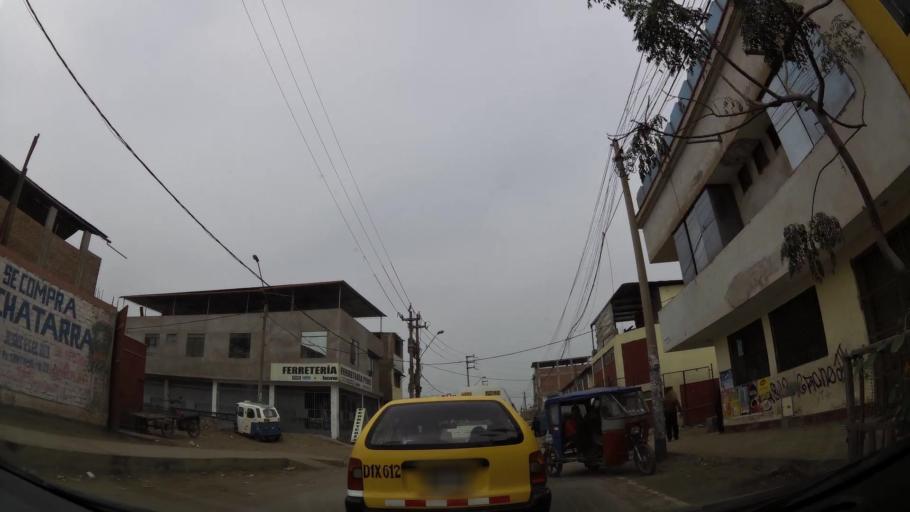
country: PE
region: Lima
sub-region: Lima
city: Surco
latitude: -12.2403
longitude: -76.9327
